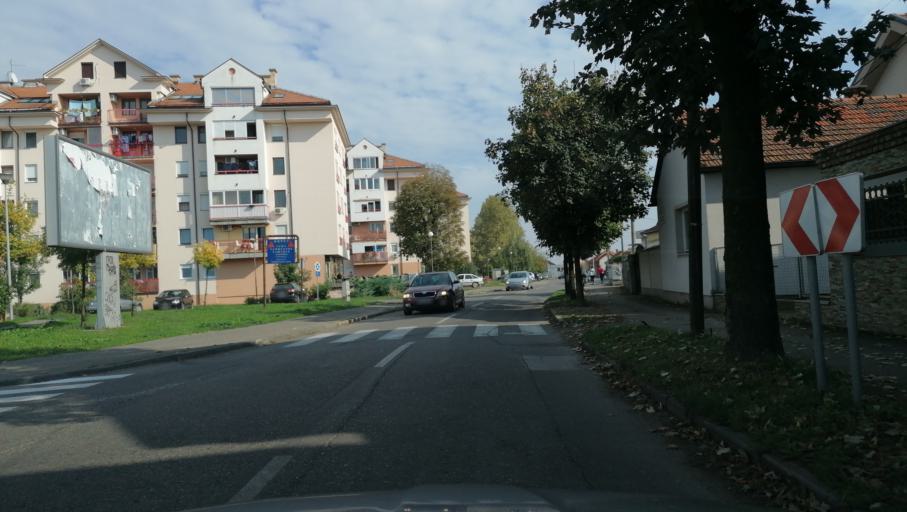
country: BA
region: Republika Srpska
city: Bijeljina
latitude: 44.7582
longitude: 19.2254
